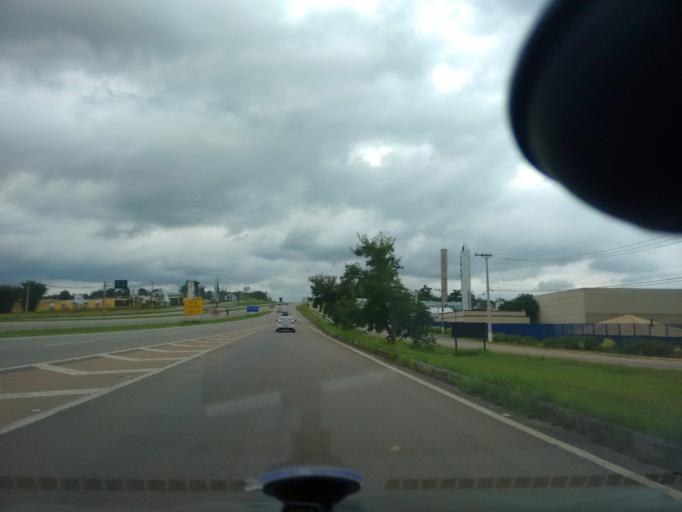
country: BR
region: Sao Paulo
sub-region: Indaiatuba
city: Indaiatuba
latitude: -23.0856
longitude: -47.1773
